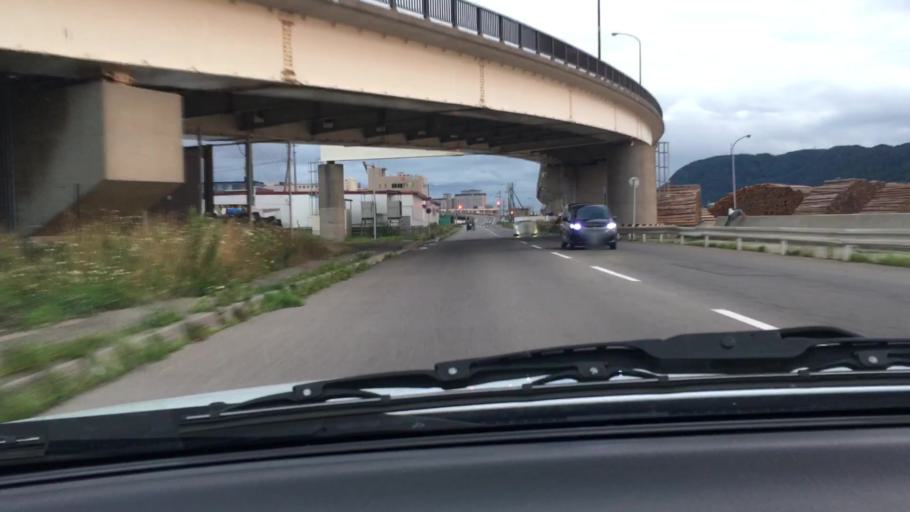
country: JP
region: Hokkaido
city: Hakodate
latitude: 41.7853
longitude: 140.7272
